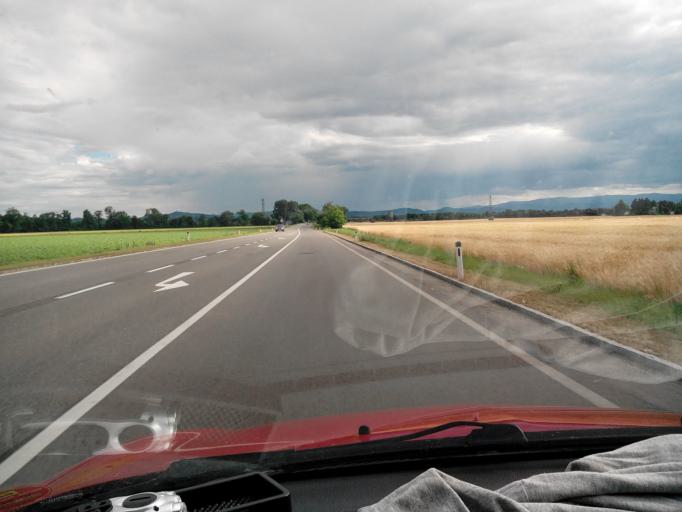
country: AT
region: Lower Austria
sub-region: Wiener Neustadt Stadt
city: Wiener Neustadt
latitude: 47.7948
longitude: 16.2379
